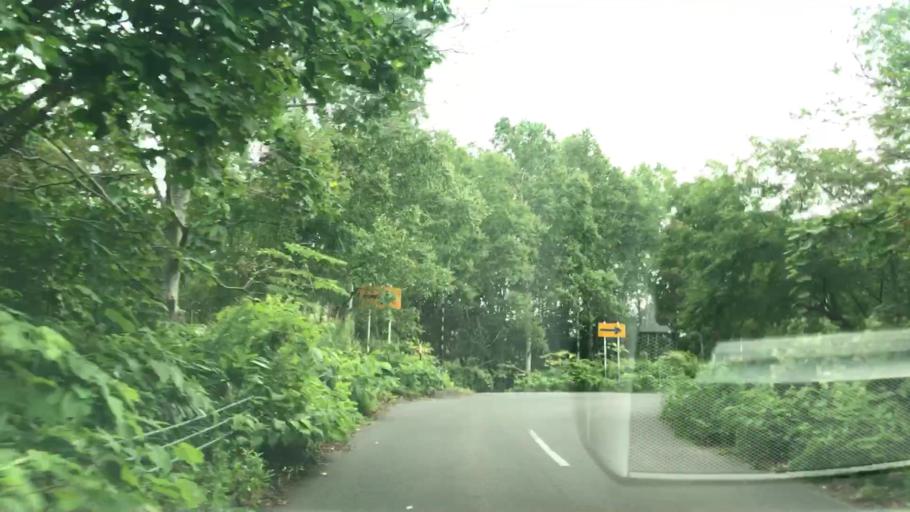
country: JP
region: Hokkaido
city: Yoichi
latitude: 43.1361
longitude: 140.8234
